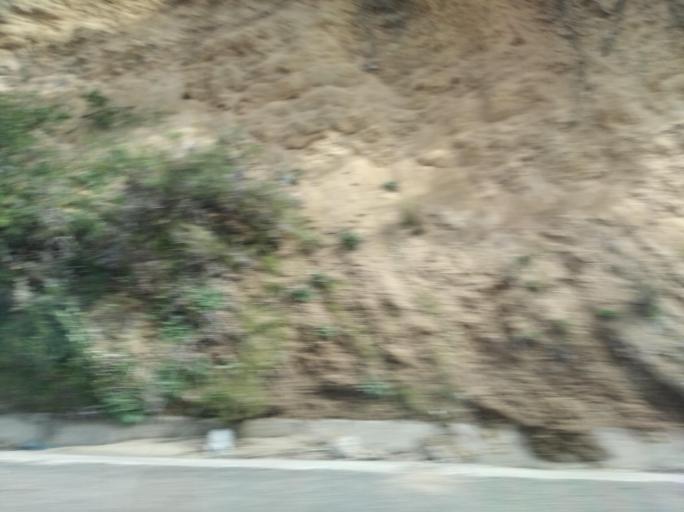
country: CL
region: Valparaiso
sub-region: Provincia de San Felipe
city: Llaillay
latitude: -33.0568
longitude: -71.0044
